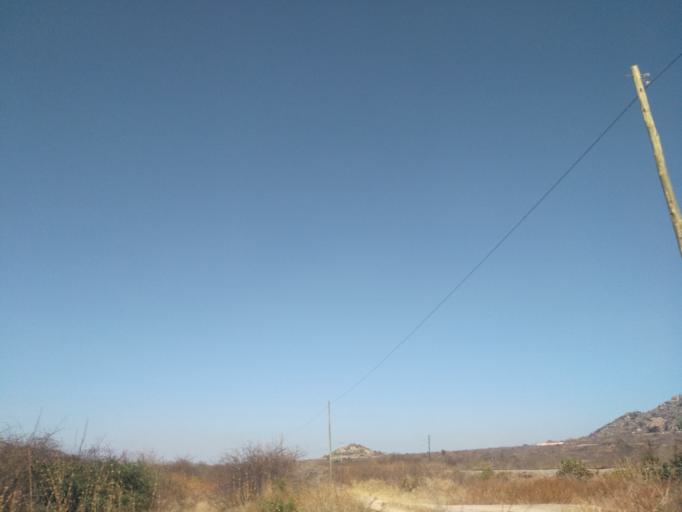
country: TZ
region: Dodoma
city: Dodoma
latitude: -6.1742
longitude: 35.7011
